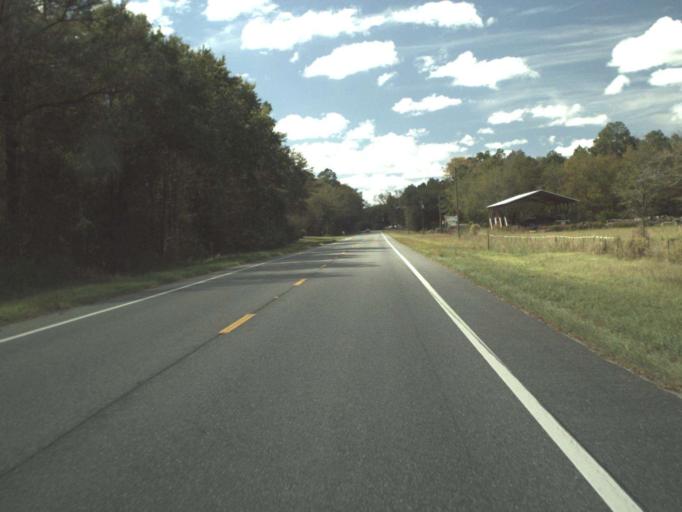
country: US
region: Florida
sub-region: Holmes County
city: Bonifay
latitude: 30.6495
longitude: -85.6778
